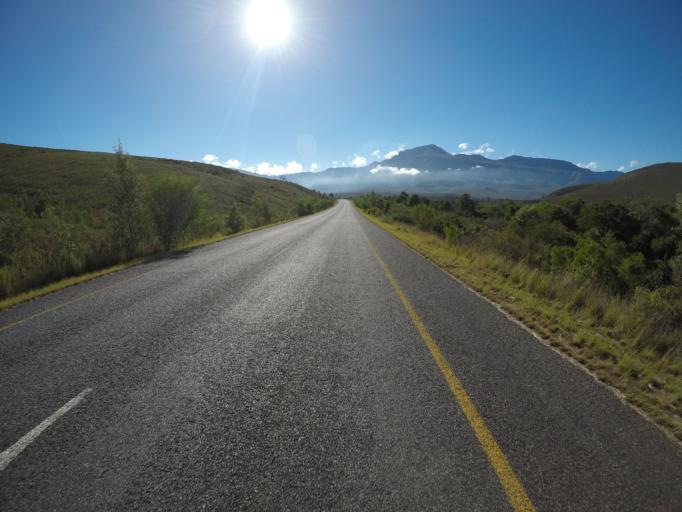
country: ZA
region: Western Cape
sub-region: Overberg District Municipality
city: Caledon
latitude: -34.0735
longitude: 19.5586
